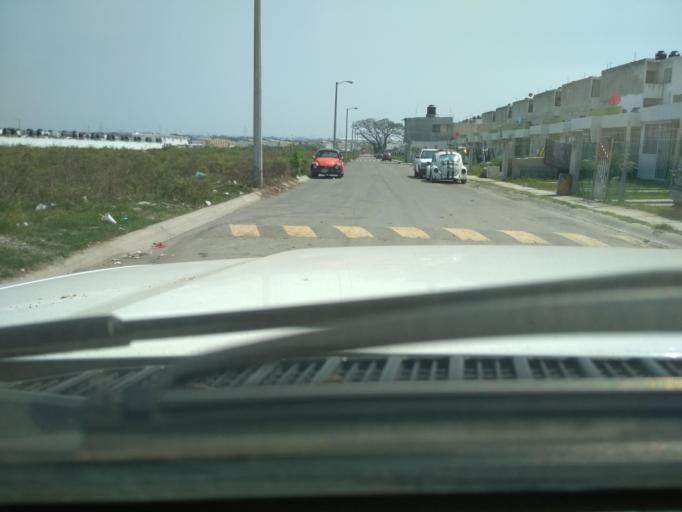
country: MX
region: Veracruz
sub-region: Veracruz
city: Lomas de Rio Medio Cuatro
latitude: 19.1867
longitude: -96.2118
